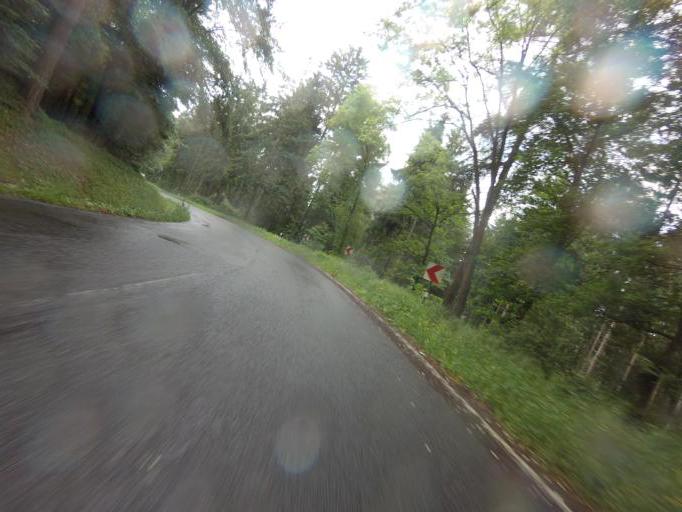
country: DE
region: Rheinland-Pfalz
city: Wirft
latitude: 50.3784
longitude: 6.8706
